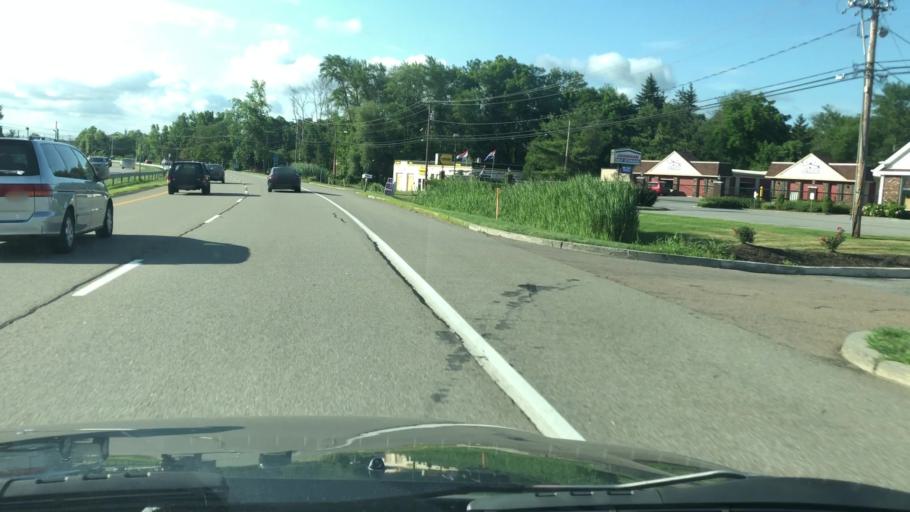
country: US
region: New York
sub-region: Dutchess County
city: Fishkill
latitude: 41.5614
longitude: -73.9035
